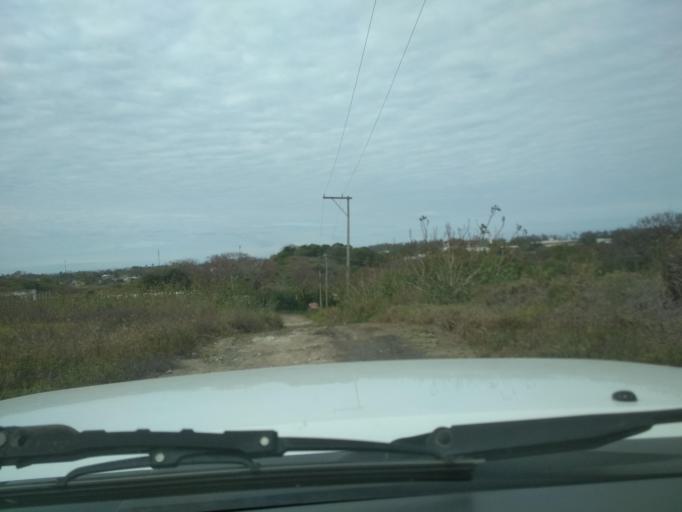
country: MX
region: Veracruz
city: Anton Lizardo
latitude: 19.0472
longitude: -95.9876
